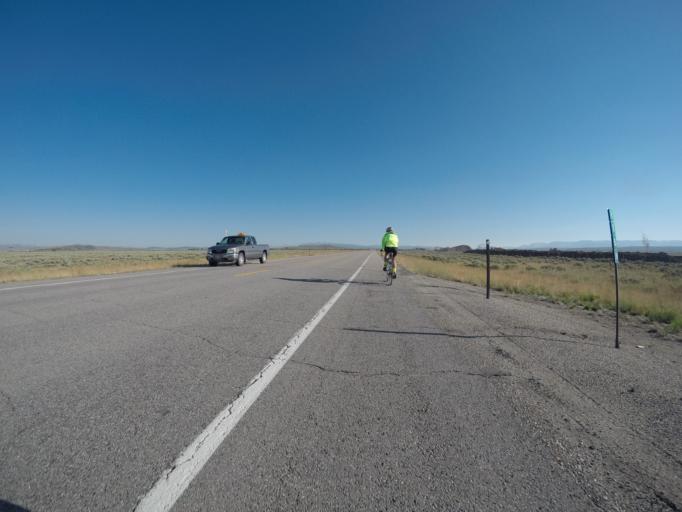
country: US
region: Wyoming
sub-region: Sublette County
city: Pinedale
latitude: 42.9666
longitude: -110.0889
